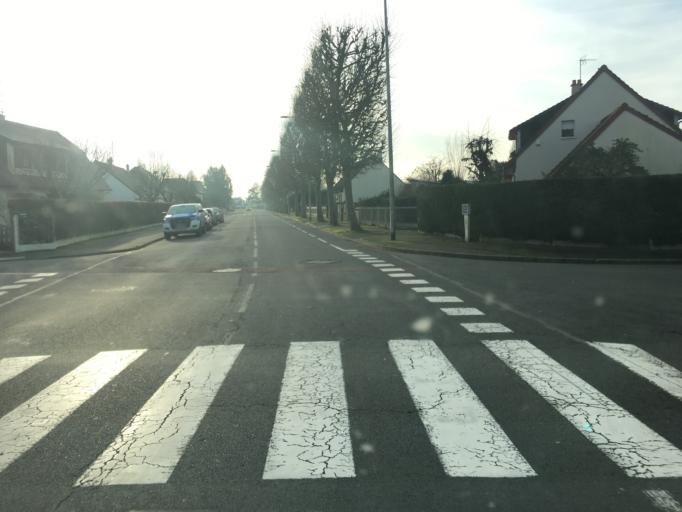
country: FR
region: Lower Normandy
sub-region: Departement du Calvados
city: Cabourg
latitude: 49.2858
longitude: -0.1168
